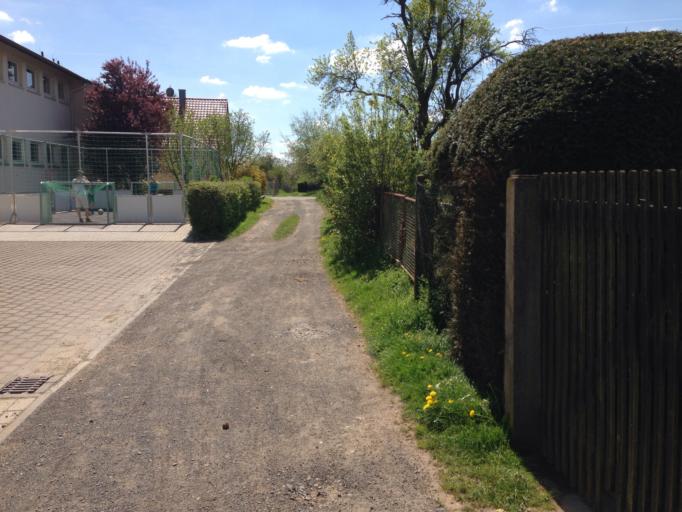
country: DE
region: Hesse
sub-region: Regierungsbezirk Giessen
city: Hungen
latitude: 50.4931
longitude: 8.8522
